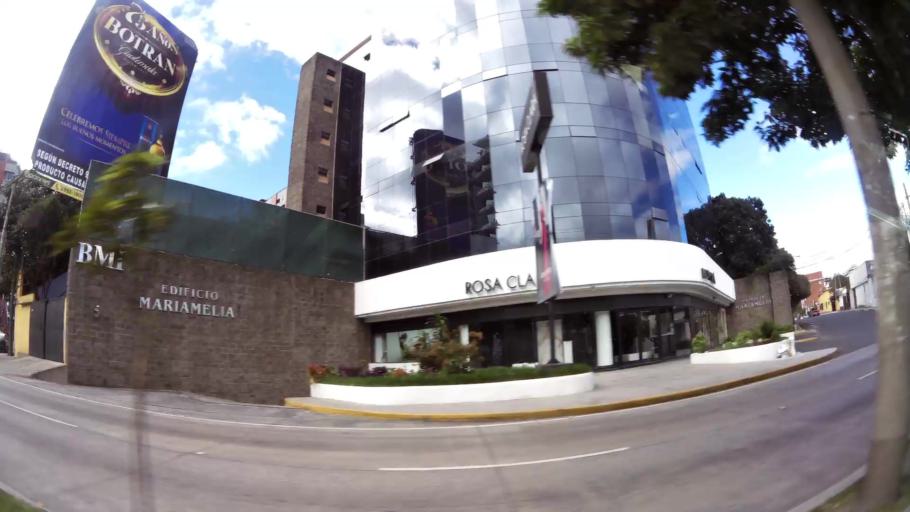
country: GT
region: Guatemala
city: Santa Catarina Pinula
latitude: 14.5923
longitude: -90.5043
